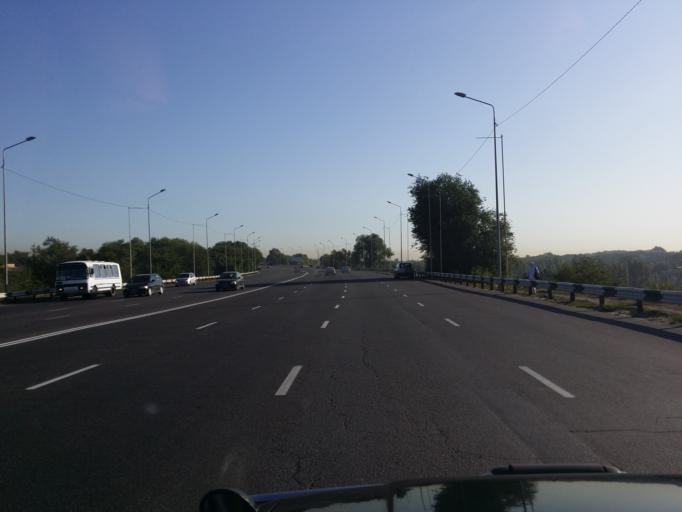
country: KZ
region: Almaty Oblysy
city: Pervomayskiy
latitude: 43.3490
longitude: 76.9359
